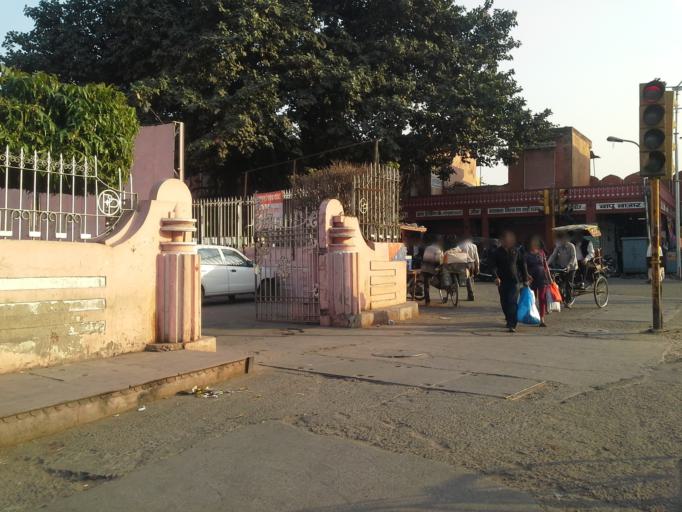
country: IN
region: Rajasthan
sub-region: Jaipur
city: Jaipur
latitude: 26.9172
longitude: 75.8209
